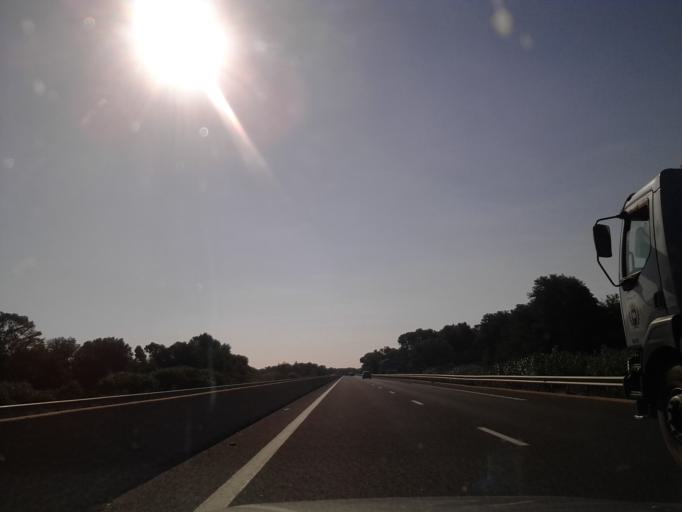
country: FR
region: Languedoc-Roussillon
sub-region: Departement des Pyrenees-Orientales
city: Corneilla-la-Riviere
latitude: 42.6911
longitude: 2.7157
